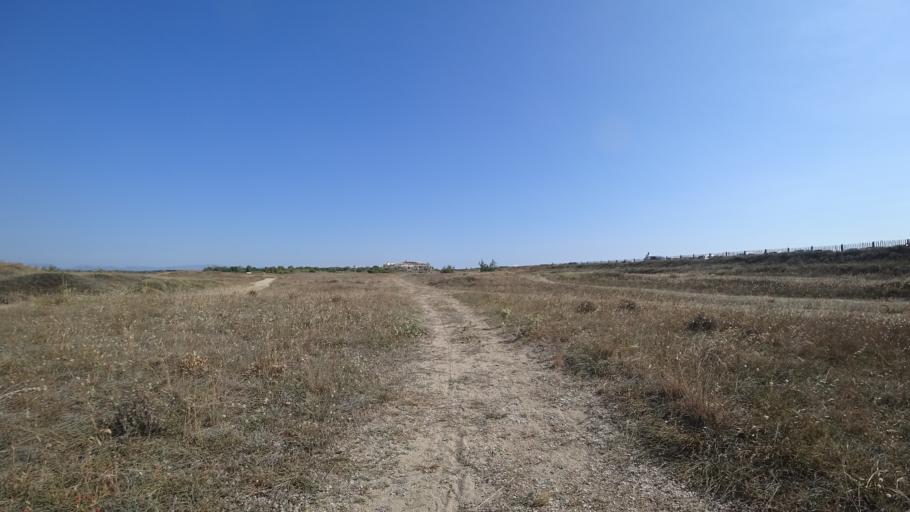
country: FR
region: Languedoc-Roussillon
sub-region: Departement des Pyrenees-Orientales
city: Canet-en-Roussillon
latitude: 42.6682
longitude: 3.0328
